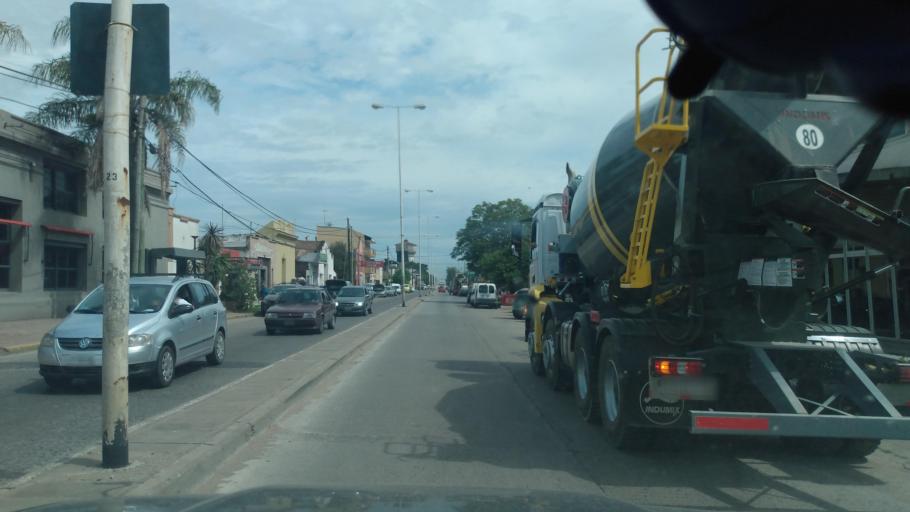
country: AR
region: Buenos Aires
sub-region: Partido de Lujan
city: Lujan
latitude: -34.5759
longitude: -59.0899
